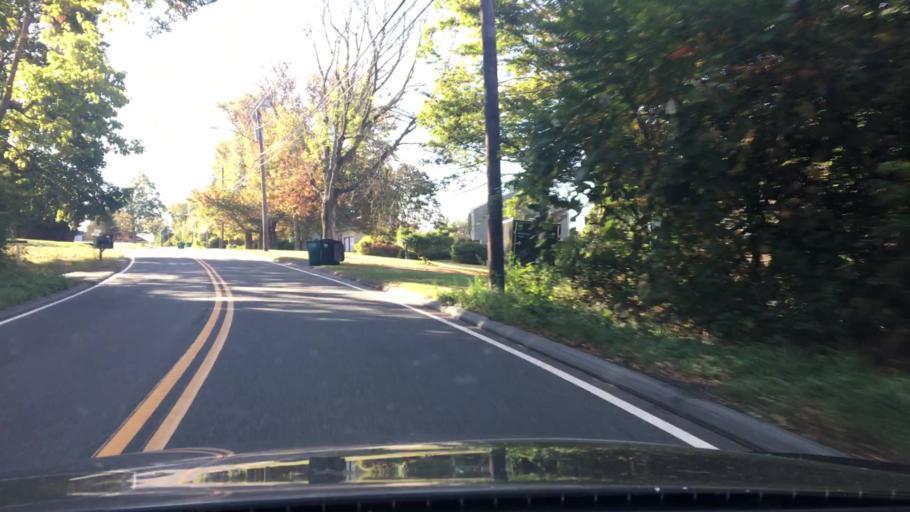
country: US
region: Connecticut
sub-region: New Haven County
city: Ansonia
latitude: 41.3659
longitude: -73.1183
